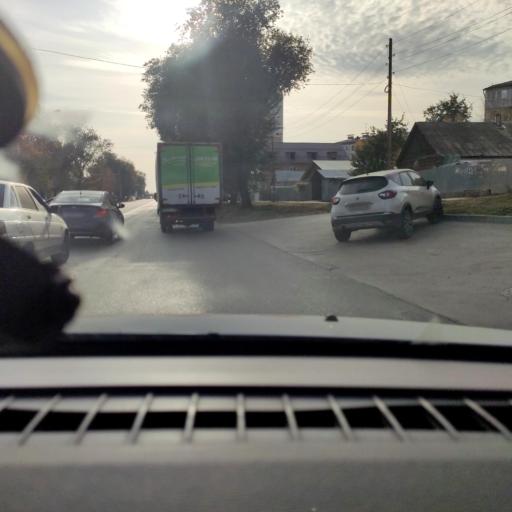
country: RU
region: Samara
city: Samara
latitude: 53.1867
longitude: 50.2051
